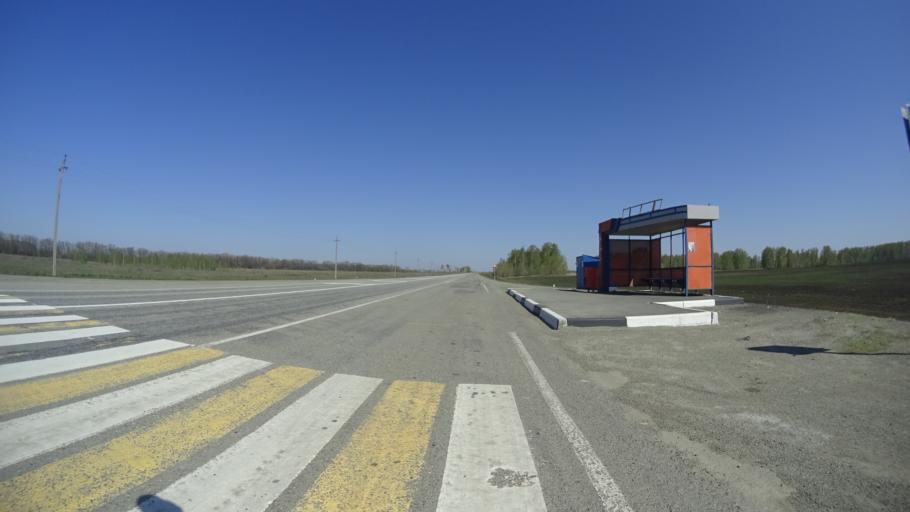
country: RU
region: Chelyabinsk
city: Troitsk
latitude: 54.1881
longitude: 61.4339
